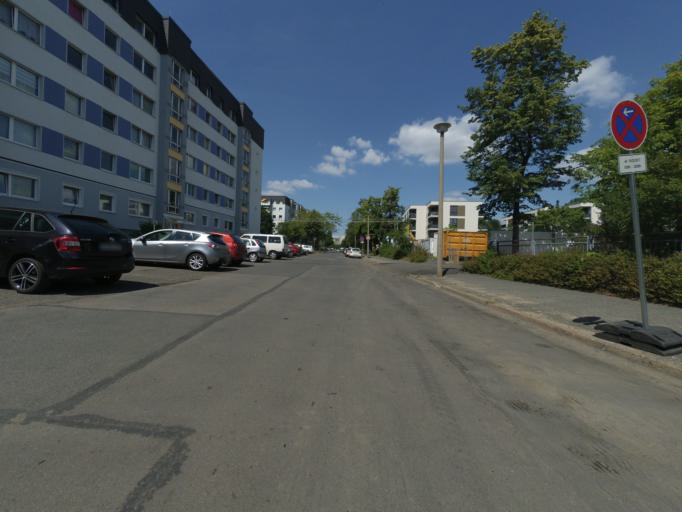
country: DE
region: Saxony
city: Albertstadt
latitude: 51.0308
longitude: 13.7942
